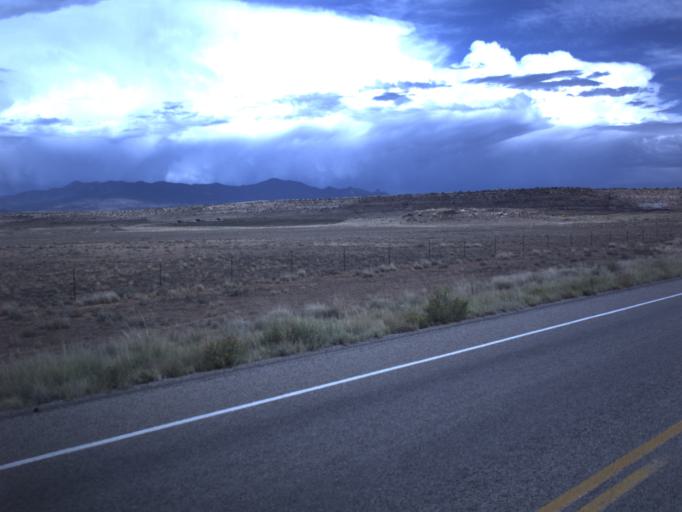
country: US
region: Colorado
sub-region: Montezuma County
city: Towaoc
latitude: 37.1706
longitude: -109.0890
